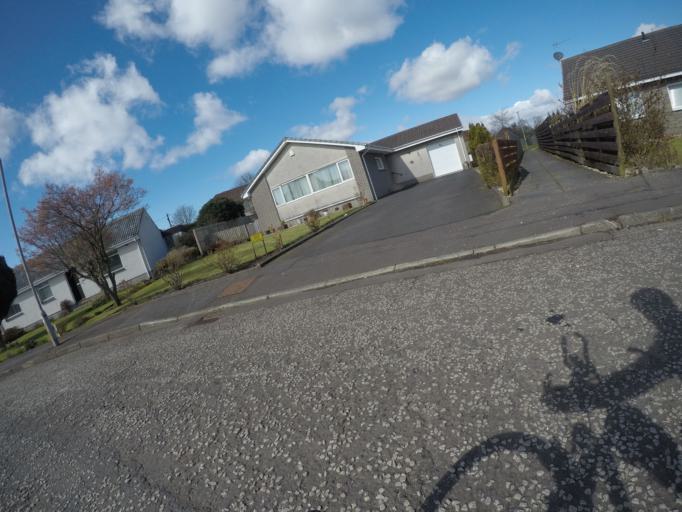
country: GB
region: Scotland
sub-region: North Ayrshire
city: Irvine
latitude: 55.6173
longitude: -4.6493
